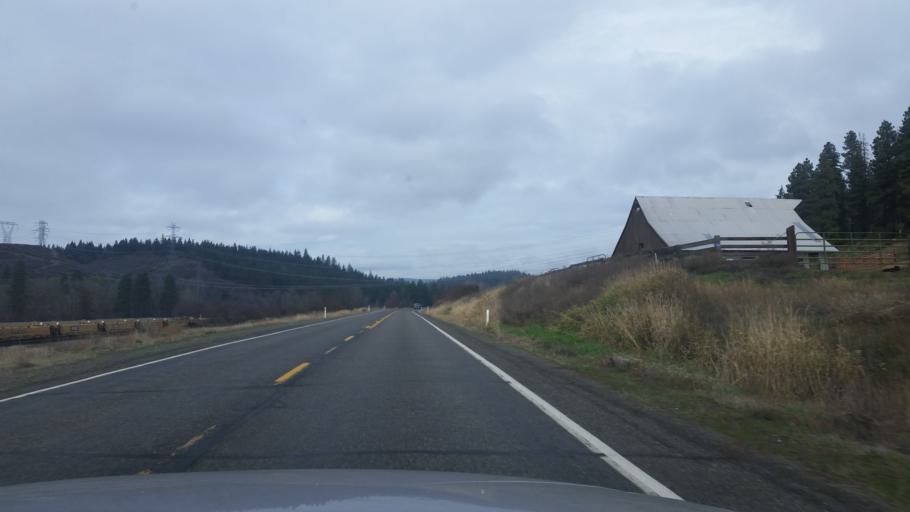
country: US
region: Washington
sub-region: Kittitas County
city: Cle Elum
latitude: 47.1497
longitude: -120.8027
